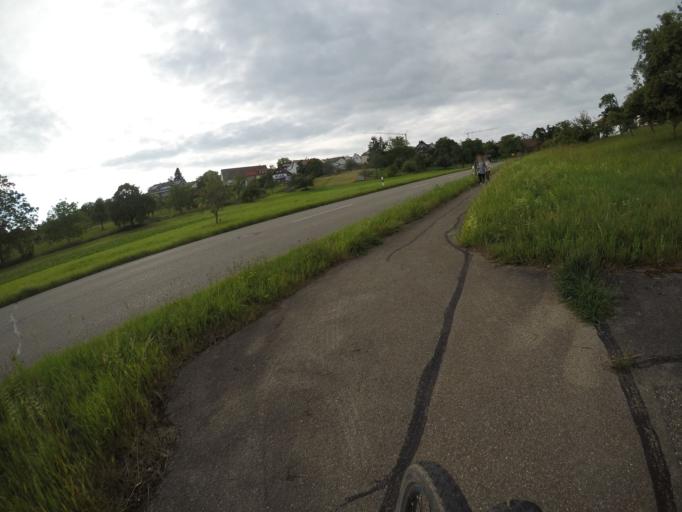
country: DE
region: Baden-Wuerttemberg
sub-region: Regierungsbezirk Stuttgart
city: Schlaitdorf
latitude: 48.6016
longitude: 9.2214
